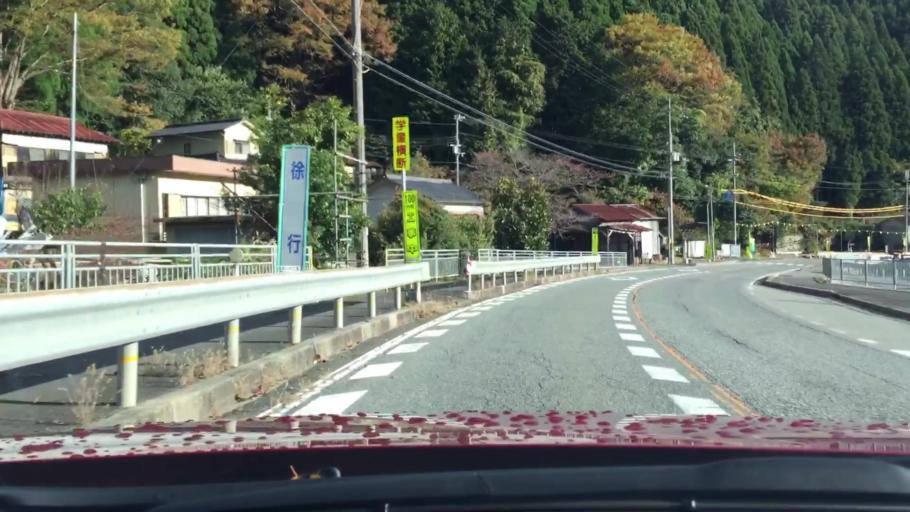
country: JP
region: Hyogo
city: Yamazakicho-nakabirose
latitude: 35.1726
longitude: 134.5440
